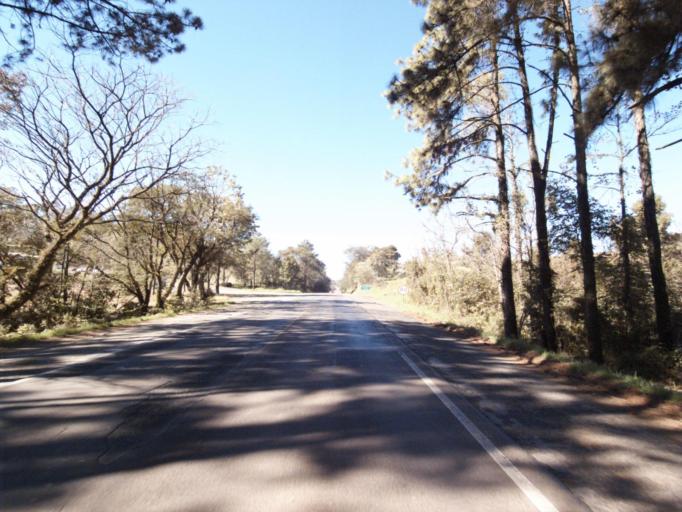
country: BR
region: Santa Catarina
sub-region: Sao Lourenco Do Oeste
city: Sao Lourenco dOeste
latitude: -26.7617
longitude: -53.2214
